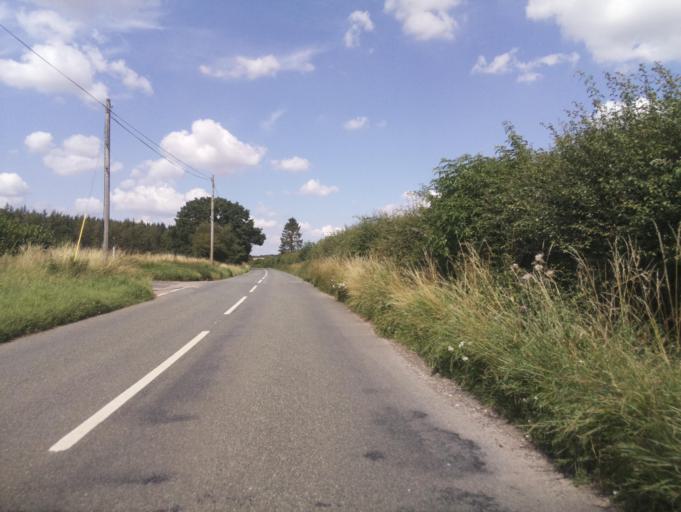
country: GB
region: England
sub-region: West Berkshire
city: Farnborough
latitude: 51.5020
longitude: -1.3656
